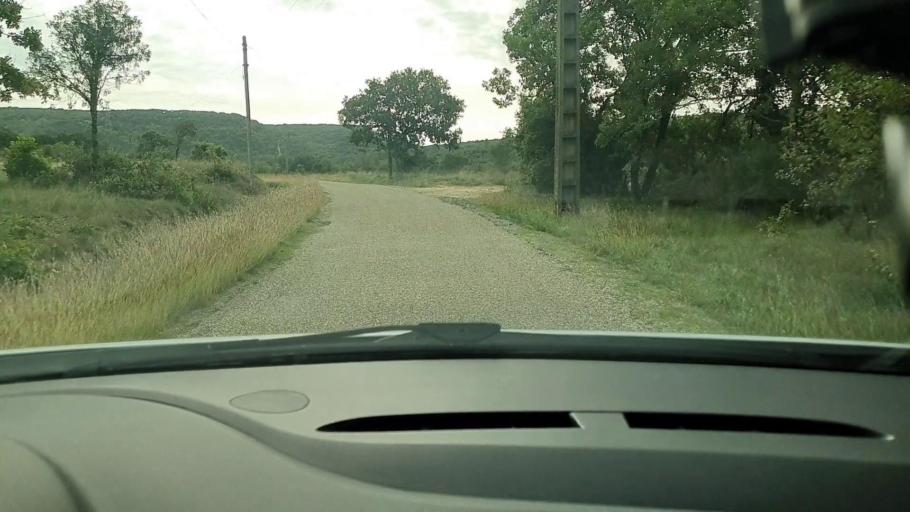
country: FR
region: Languedoc-Roussillon
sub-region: Departement du Gard
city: Montaren-et-Saint-Mediers
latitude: 44.1029
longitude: 4.3092
